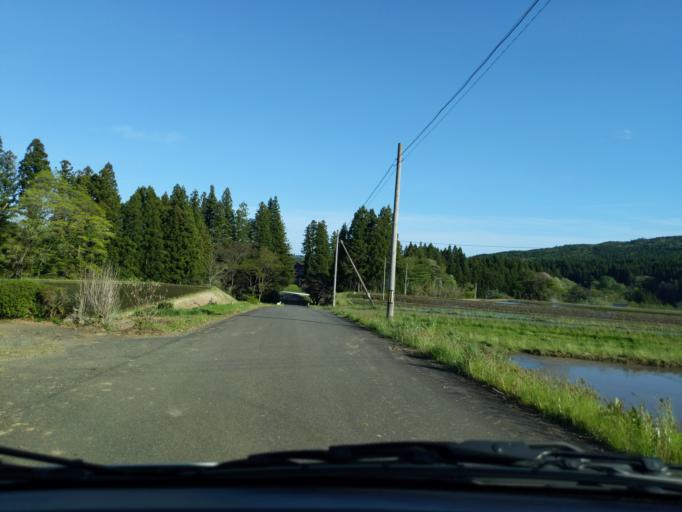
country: JP
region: Iwate
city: Ichinoseki
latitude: 38.8774
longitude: 140.8925
